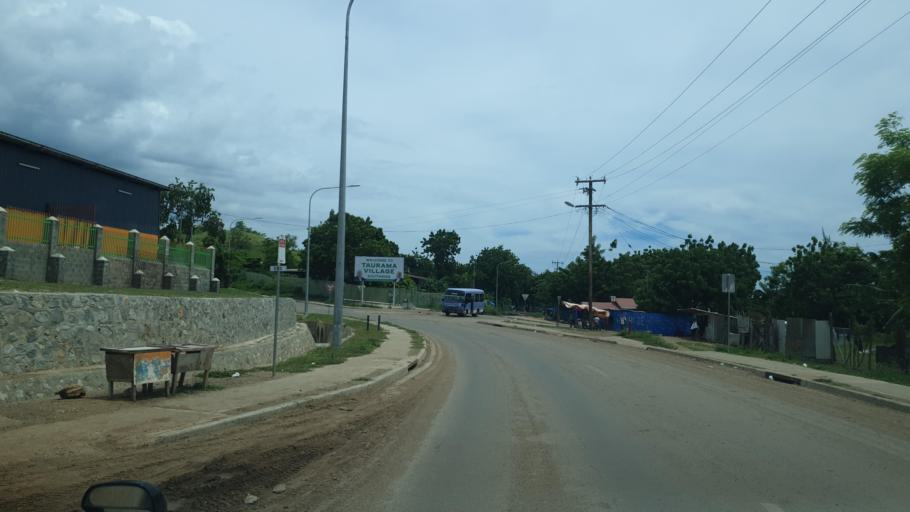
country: PG
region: National Capital
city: Port Moresby
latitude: -9.5286
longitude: 147.2426
